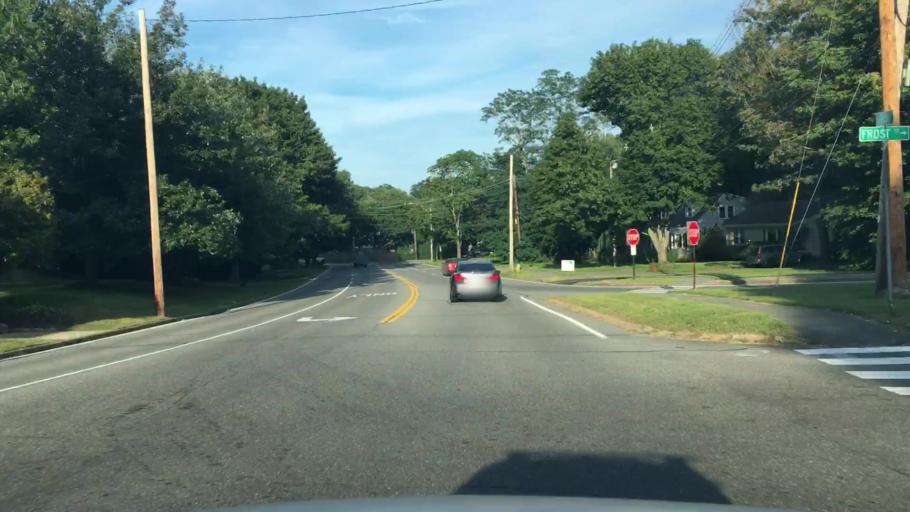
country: US
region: Maine
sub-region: Cumberland County
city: South Portland Gardens
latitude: 43.6623
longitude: -70.2999
